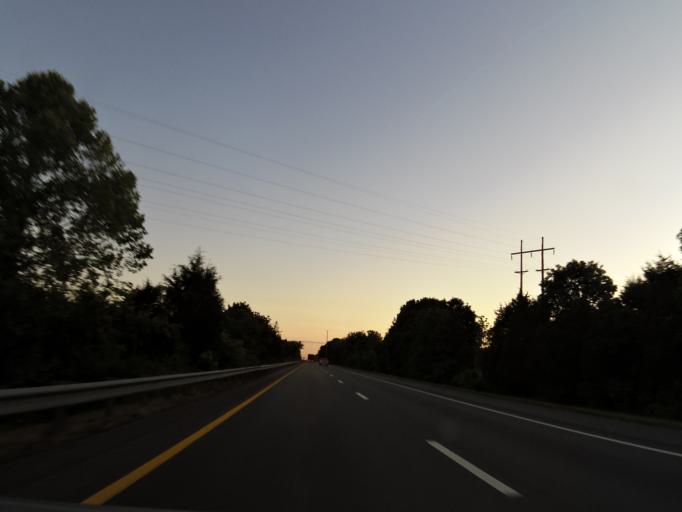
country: US
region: Tennessee
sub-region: Jefferson County
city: Dandridge
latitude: 36.0713
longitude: -83.3833
